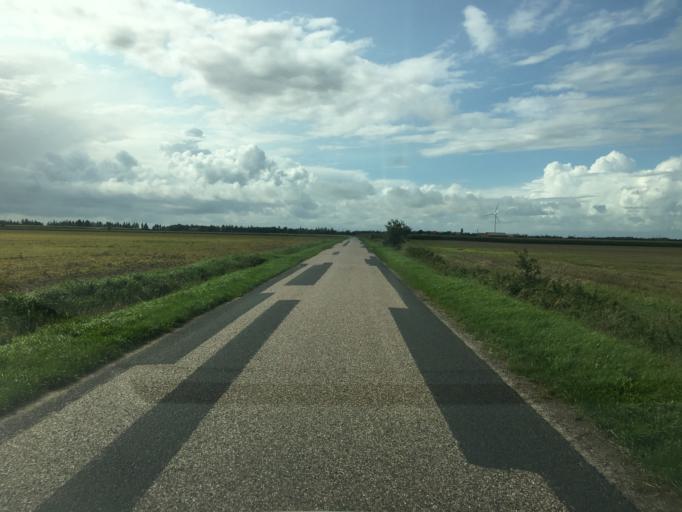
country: DK
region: South Denmark
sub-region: Tonder Kommune
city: Tonder
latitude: 54.9779
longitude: 8.8548
